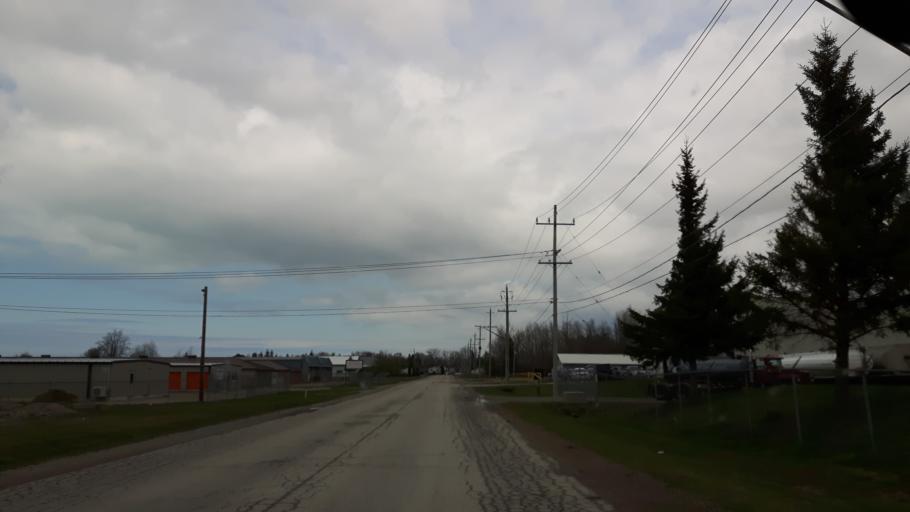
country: CA
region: Ontario
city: Goderich
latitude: 43.7275
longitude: -81.6994
